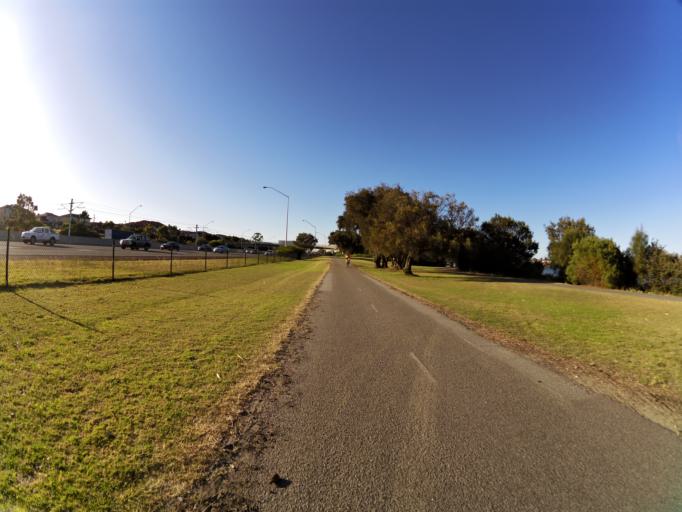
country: AU
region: Western Australia
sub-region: South Perth
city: Manning
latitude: -32.0158
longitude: 115.8572
